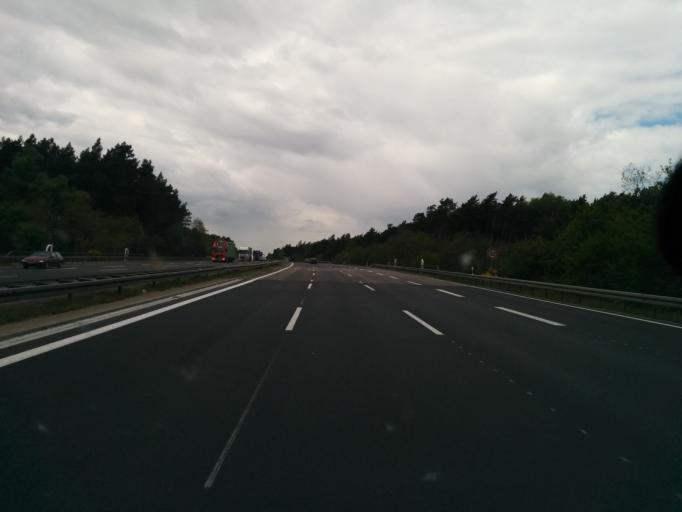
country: DE
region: Brandenburg
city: Brandenburg an der Havel
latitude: 52.3505
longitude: 12.6005
